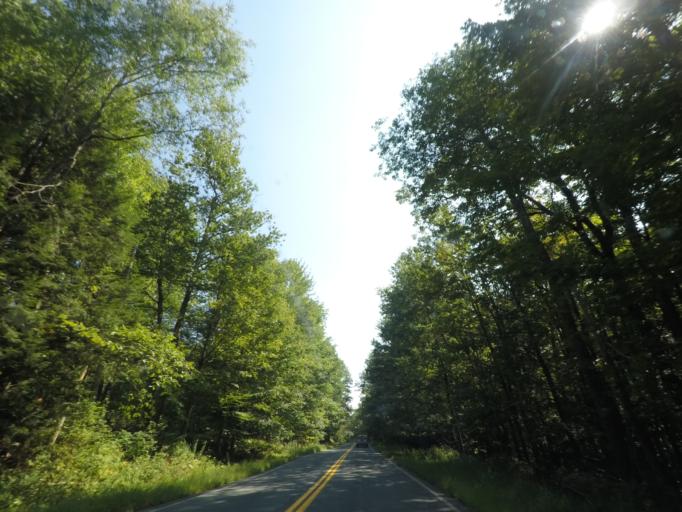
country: US
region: New York
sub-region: Rensselaer County
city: Poestenkill
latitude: 42.7210
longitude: -73.5097
